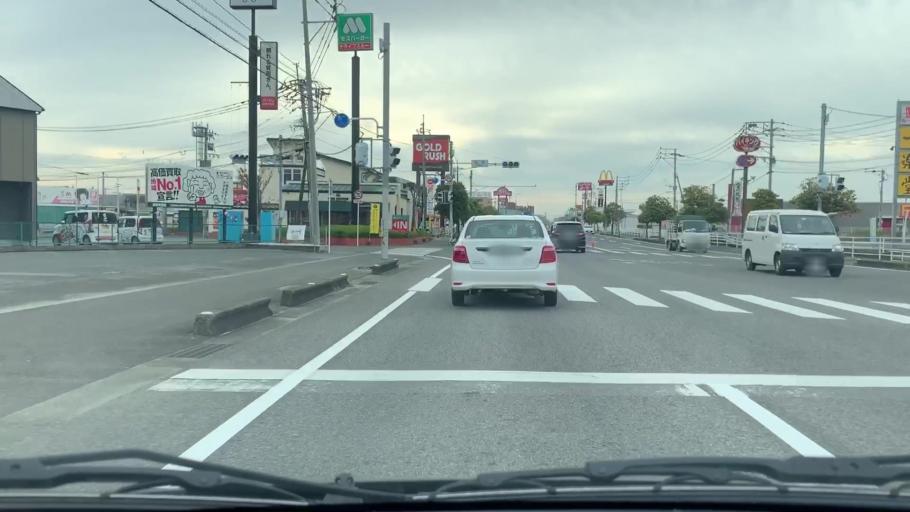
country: JP
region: Saga Prefecture
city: Saga-shi
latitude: 33.2946
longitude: 130.2839
